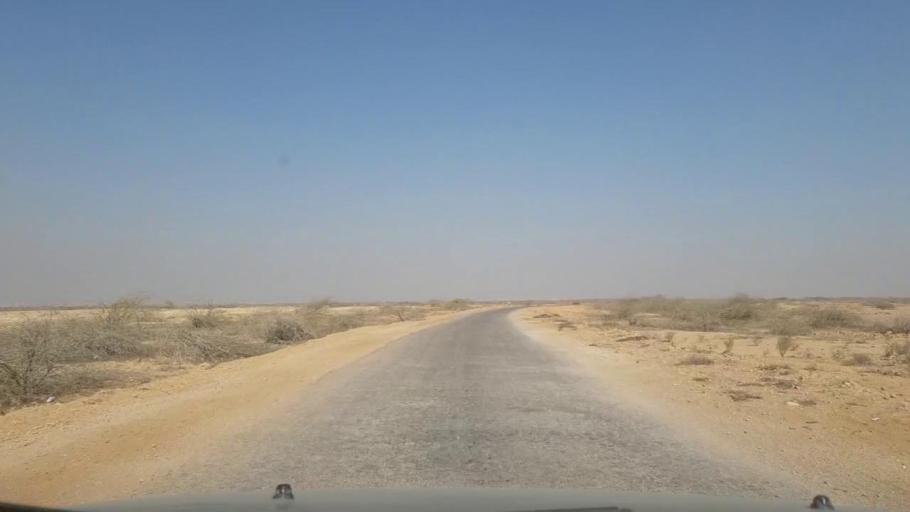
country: PK
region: Sindh
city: Thatta
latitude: 24.8400
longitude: 67.8886
